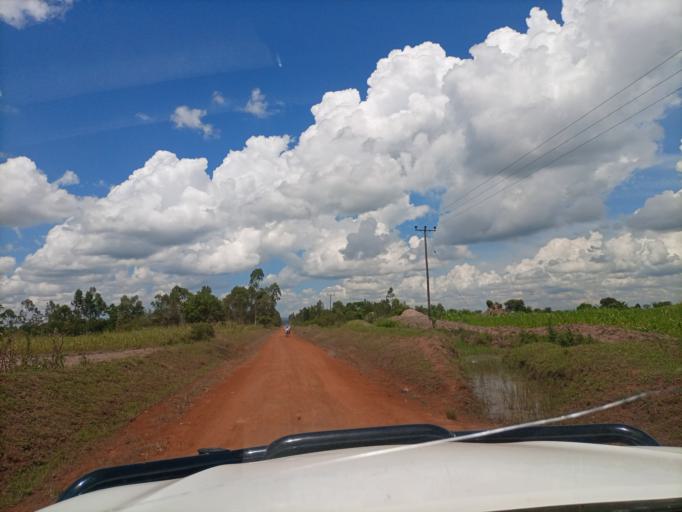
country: UG
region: Eastern Region
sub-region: Tororo District
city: Tororo
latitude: 0.6632
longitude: 34.0014
